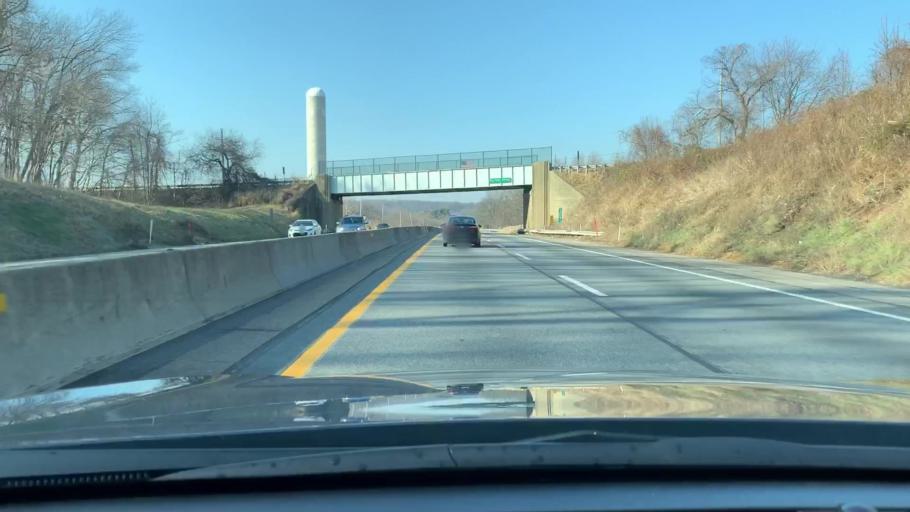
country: US
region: Pennsylvania
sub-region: Chester County
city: Downingtown
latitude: 40.0841
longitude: -75.7139
